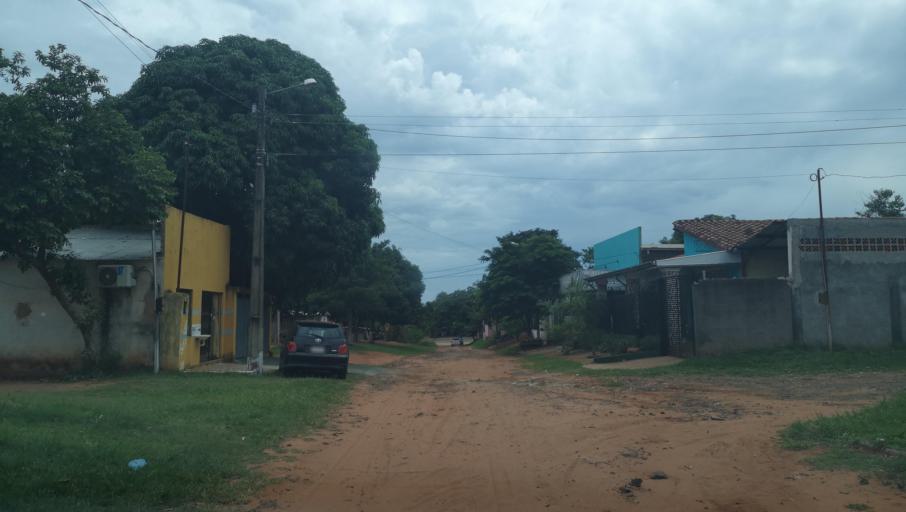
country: PY
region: San Pedro
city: Capiibary
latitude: -24.7224
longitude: -56.0147
